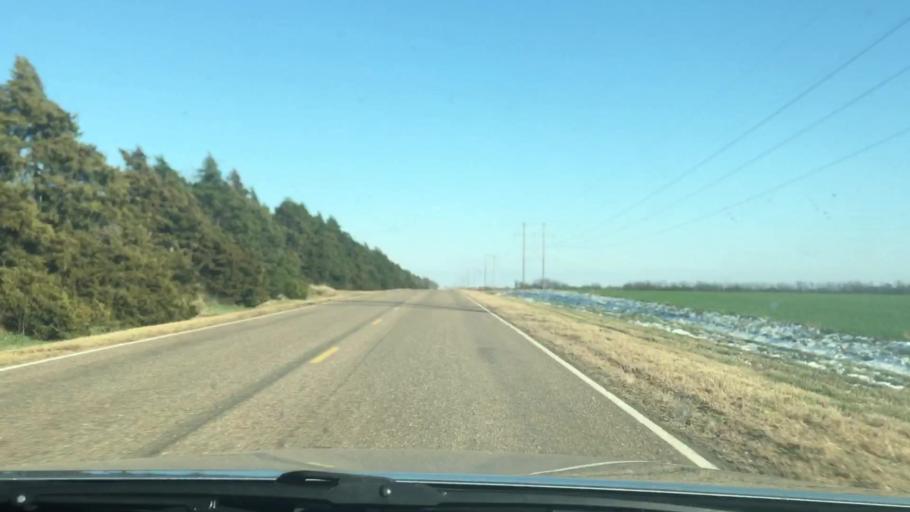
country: US
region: Kansas
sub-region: Rice County
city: Lyons
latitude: 38.2896
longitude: -98.1071
